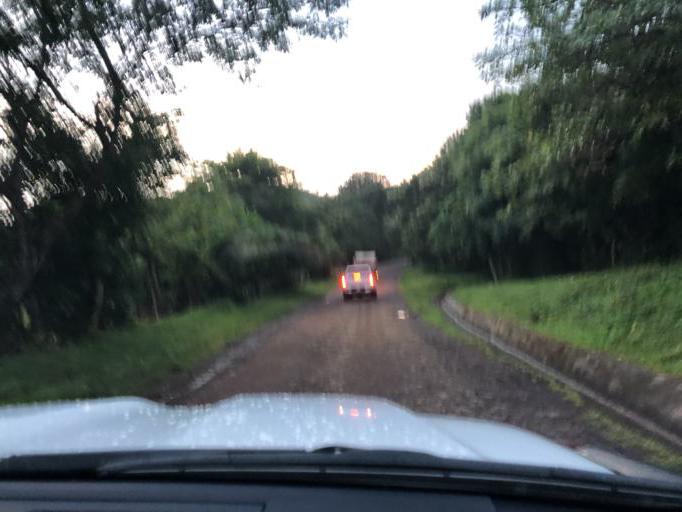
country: NI
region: Chontales
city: La Libertad
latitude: 12.1588
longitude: -85.1784
